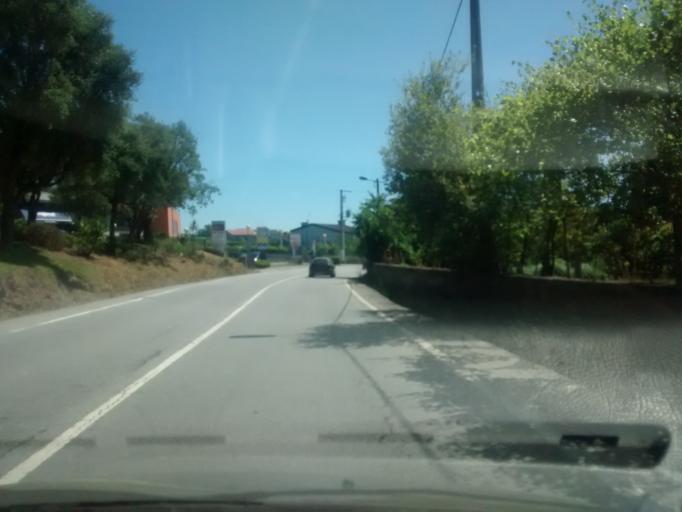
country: PT
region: Braga
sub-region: Barcelos
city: Galegos
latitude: 41.5240
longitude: -8.5662
